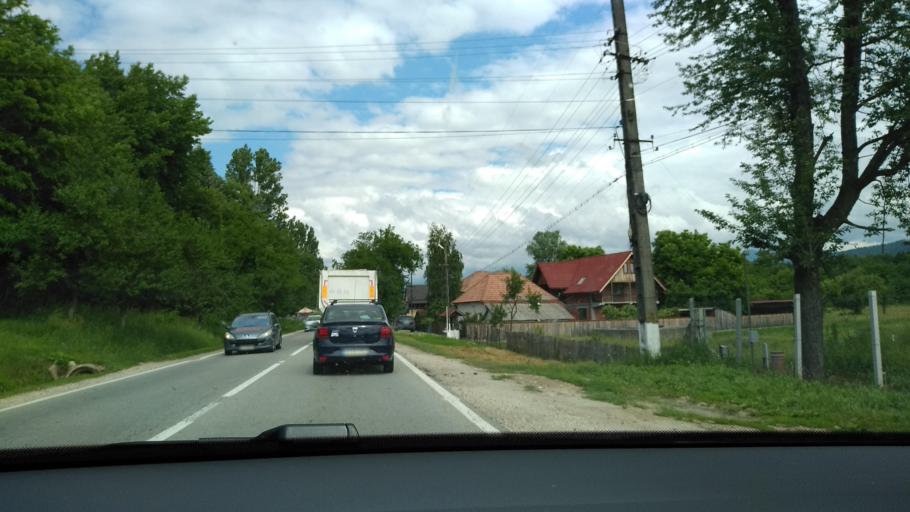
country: RO
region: Valcea
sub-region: Comuna Tomsani
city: Tomsani
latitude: 45.1305
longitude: 24.0351
